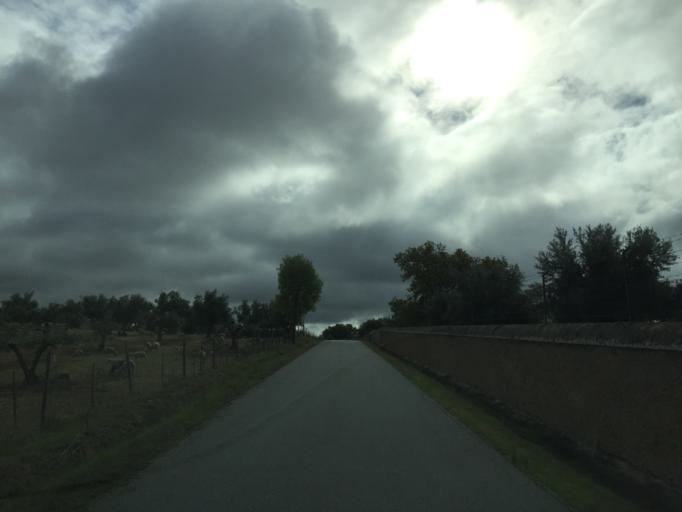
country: PT
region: Portalegre
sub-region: Alter do Chao
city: Alter do Chao
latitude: 39.2262
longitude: -7.6788
